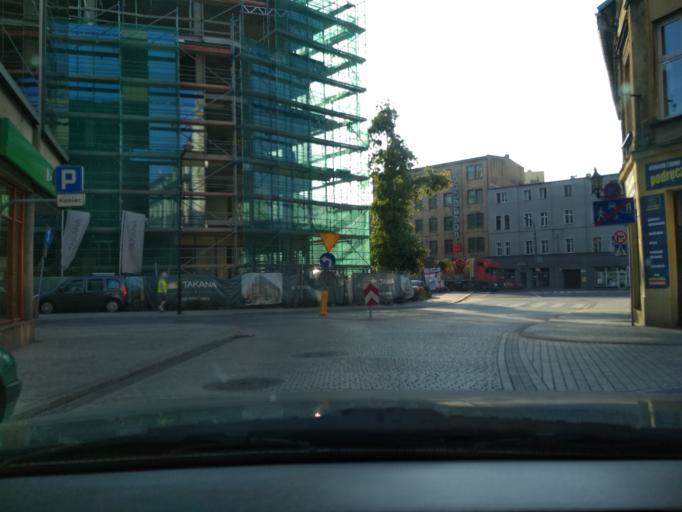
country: PL
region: Silesian Voivodeship
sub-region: Gliwice
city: Gliwice
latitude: 50.2934
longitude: 18.6683
